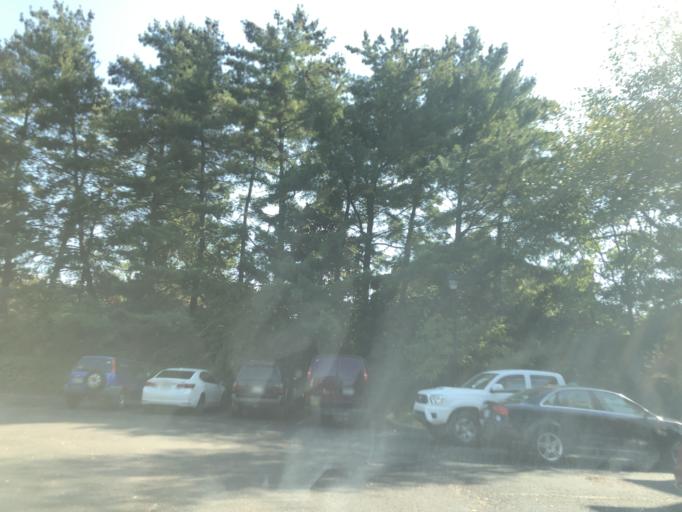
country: US
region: Tennessee
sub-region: Davidson County
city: Forest Hills
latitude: 36.0924
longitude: -86.8182
